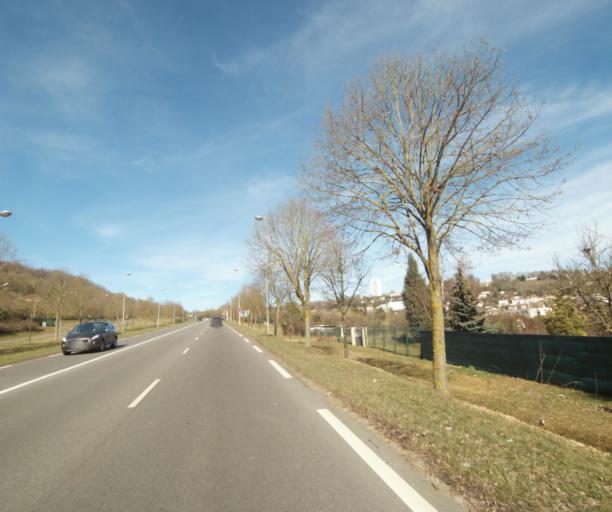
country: FR
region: Lorraine
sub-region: Departement de Meurthe-et-Moselle
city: Laxou
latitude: 48.6818
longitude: 6.1408
